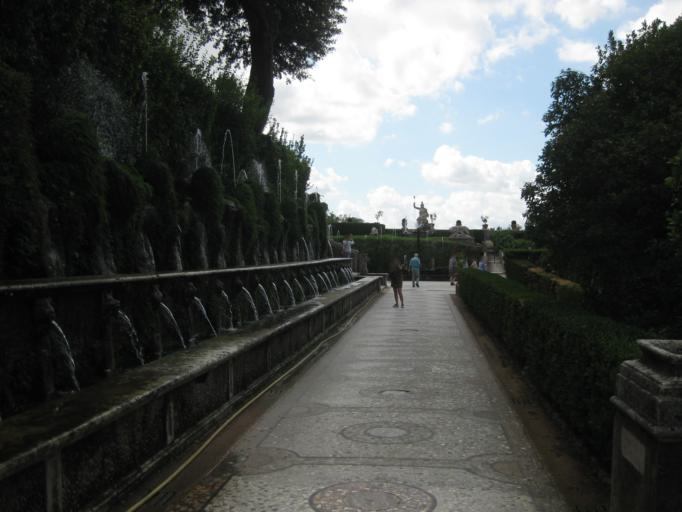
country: IT
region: Latium
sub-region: Citta metropolitana di Roma Capitale
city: Tivoli
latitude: 41.9627
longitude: 12.7957
